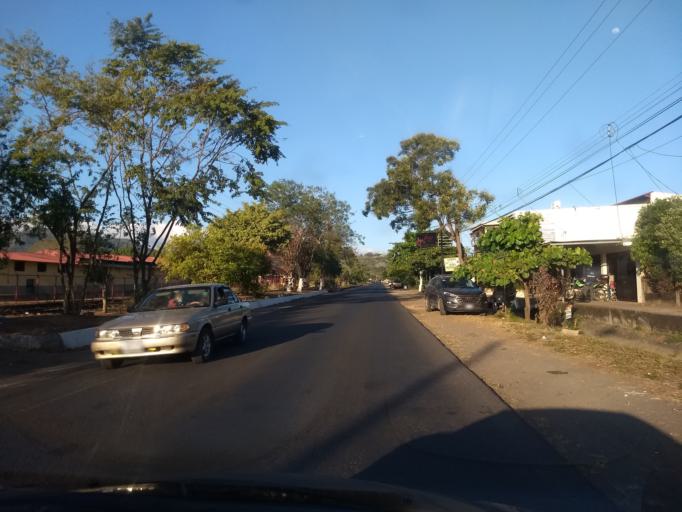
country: CR
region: Puntarenas
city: Esparza
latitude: 9.9857
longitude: -84.7172
